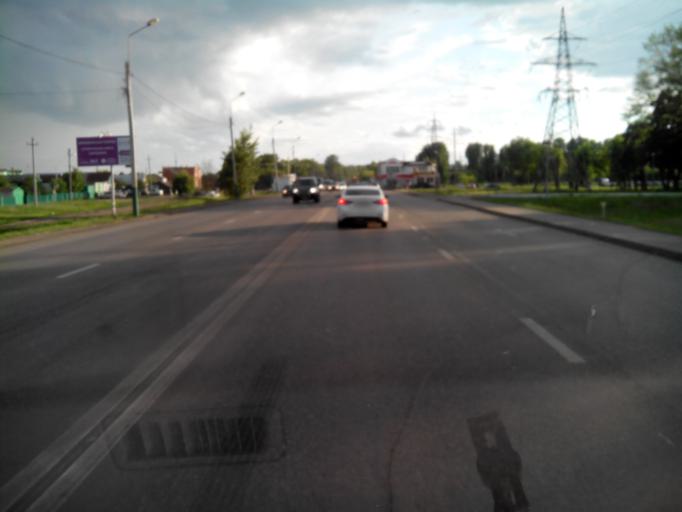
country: RU
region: Penza
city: Penza
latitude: 53.1525
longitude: 44.9719
